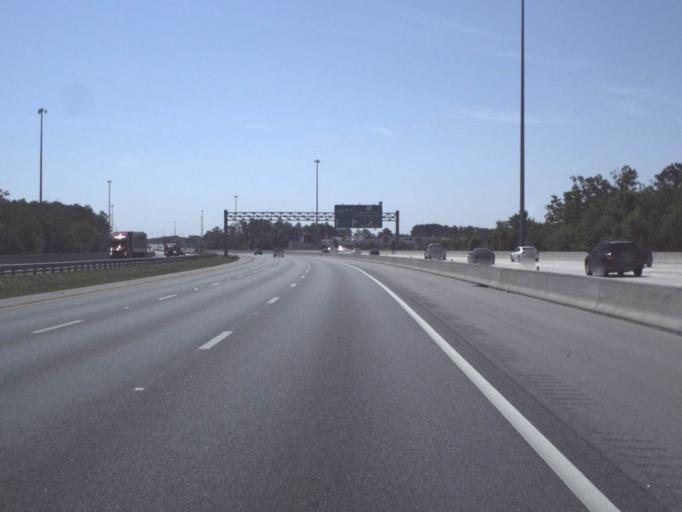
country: US
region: Florida
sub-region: Clay County
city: Bellair-Meadowbrook Terrace
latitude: 30.2022
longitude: -81.7531
